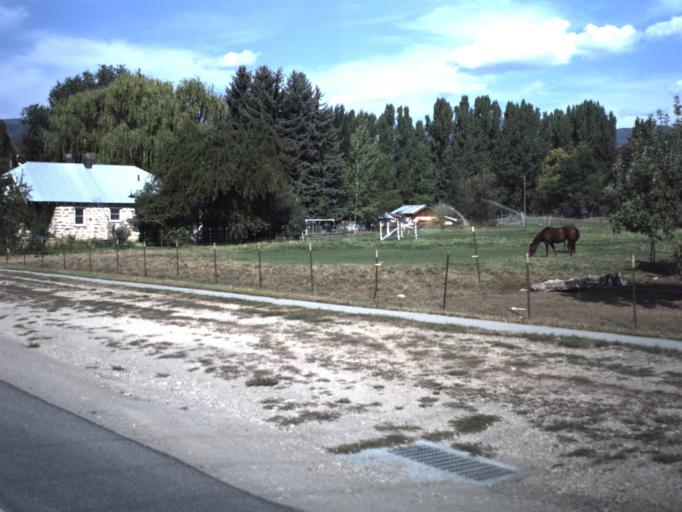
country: US
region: Utah
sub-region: Wasatch County
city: Midway
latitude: 40.5121
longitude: -111.4639
